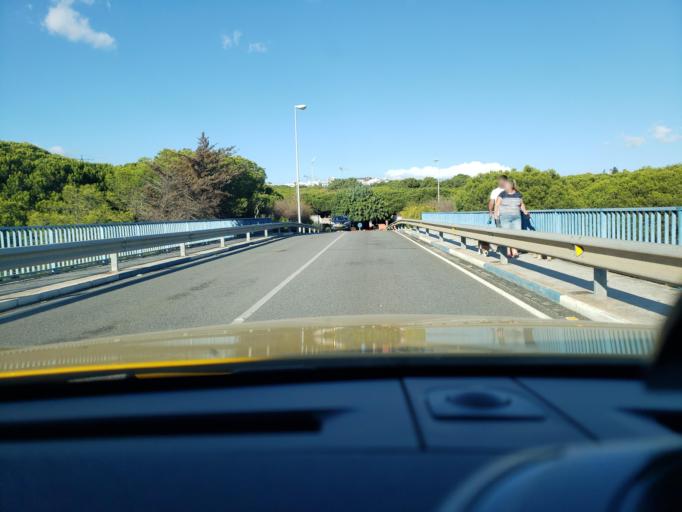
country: ES
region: Andalusia
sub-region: Provincia de Malaga
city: Fuengirola
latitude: 36.4880
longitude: -4.7433
